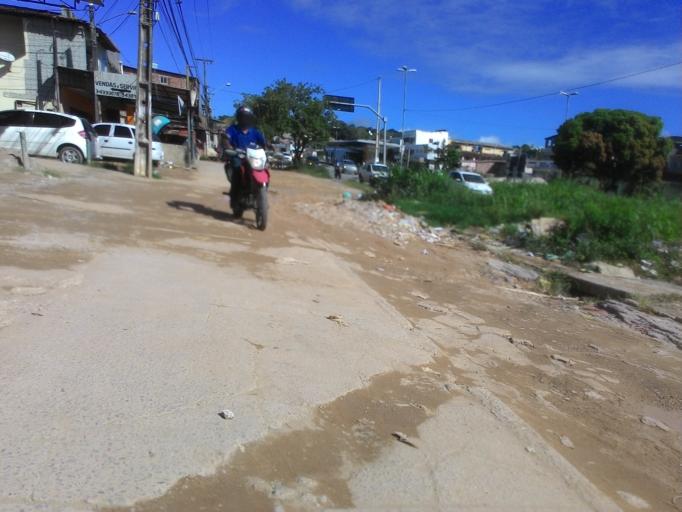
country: BR
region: Pernambuco
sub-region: Paulista
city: Paulista
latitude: -7.9741
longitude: -34.8642
